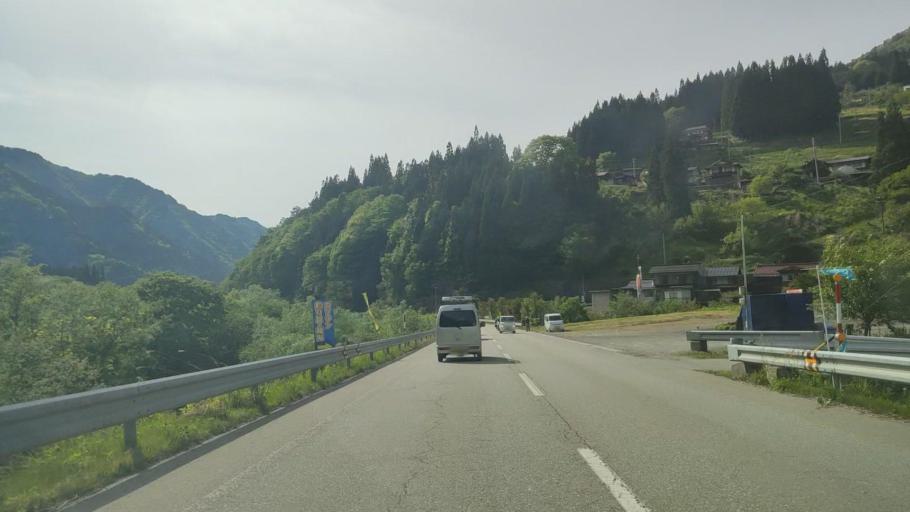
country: JP
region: Gifu
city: Takayama
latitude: 36.2690
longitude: 137.4057
